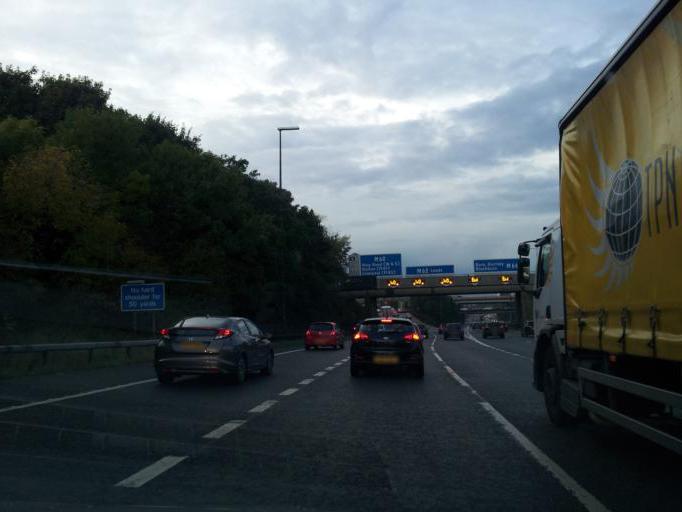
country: GB
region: England
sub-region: Borough of Bury
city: Prestwich
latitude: 53.5469
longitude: -2.2573
